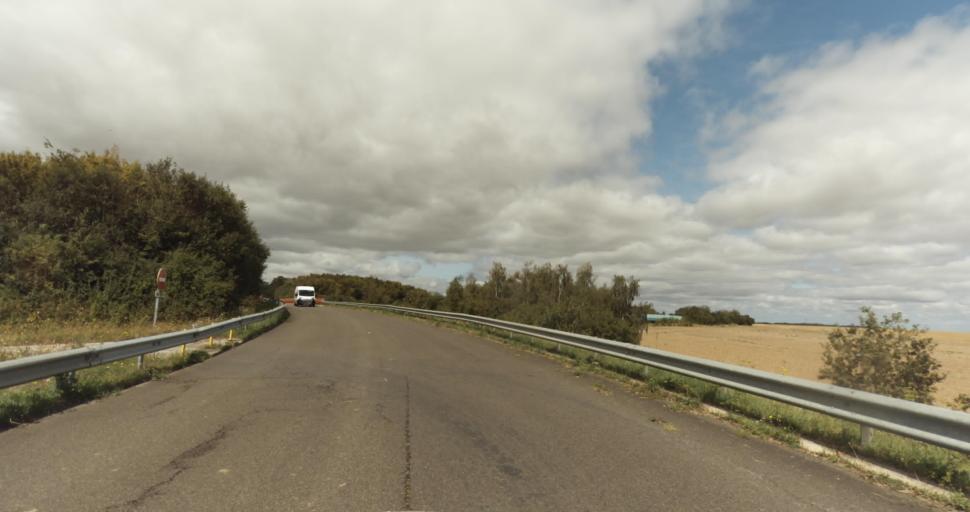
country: FR
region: Haute-Normandie
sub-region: Departement de l'Eure
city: Evreux
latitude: 48.9250
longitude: 1.2056
